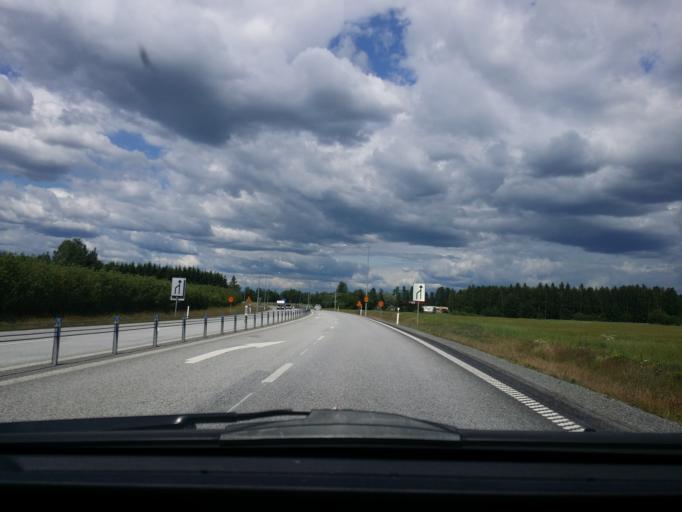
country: SE
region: OErebro
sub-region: Orebro Kommun
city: Hovsta
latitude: 59.4205
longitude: 15.1788
